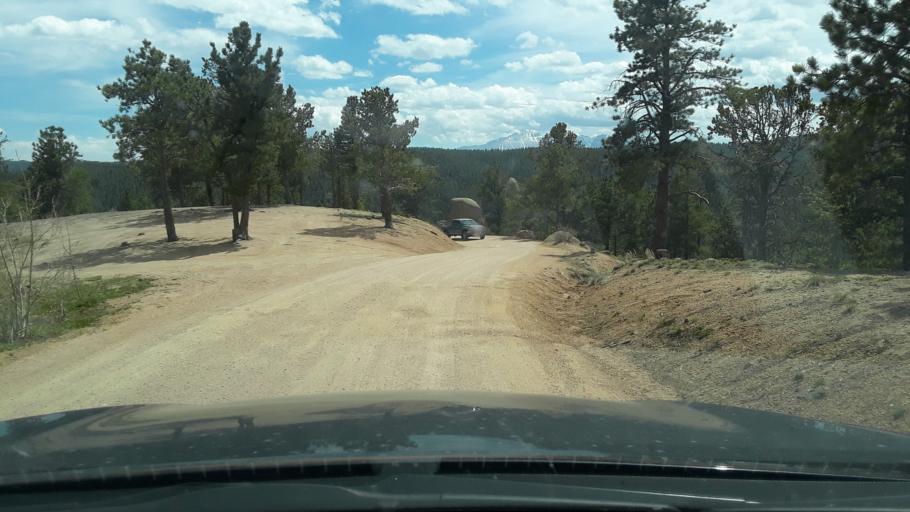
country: US
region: Colorado
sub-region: El Paso County
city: Palmer Lake
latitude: 39.0691
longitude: -104.9496
